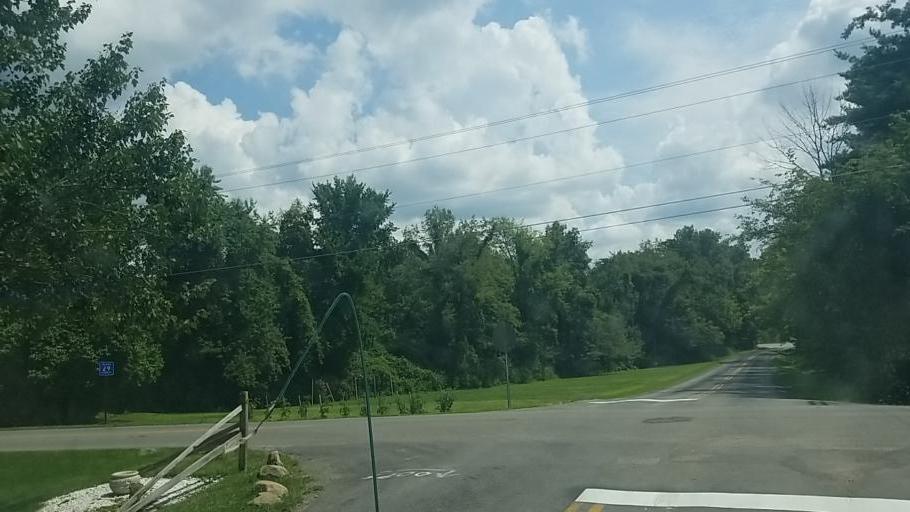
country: US
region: Ohio
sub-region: Medina County
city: Lodi
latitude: 41.0140
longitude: -82.0548
